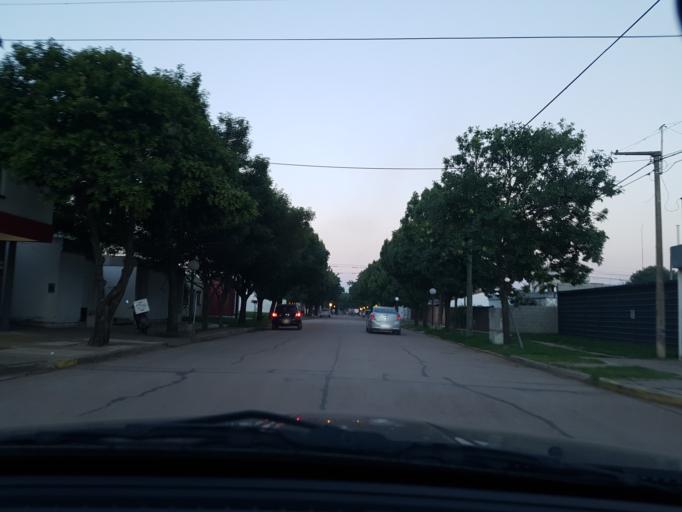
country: AR
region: Cordoba
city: General Cabrera
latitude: -32.7583
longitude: -63.7949
